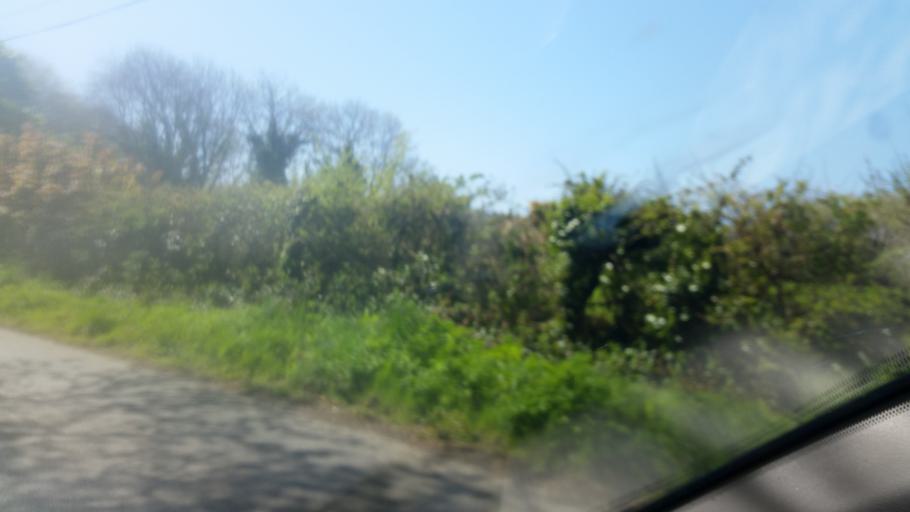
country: IE
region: Munster
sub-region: Waterford
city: Dunmore East
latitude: 52.2129
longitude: -6.8596
